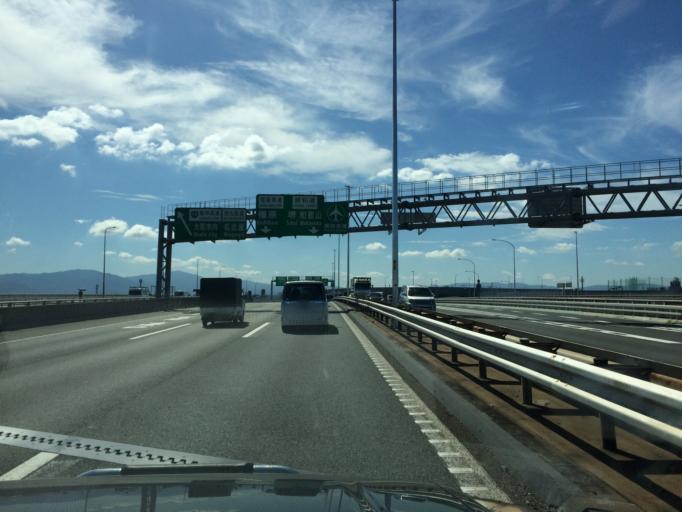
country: JP
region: Osaka
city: Yao
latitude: 34.5947
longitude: 135.5753
